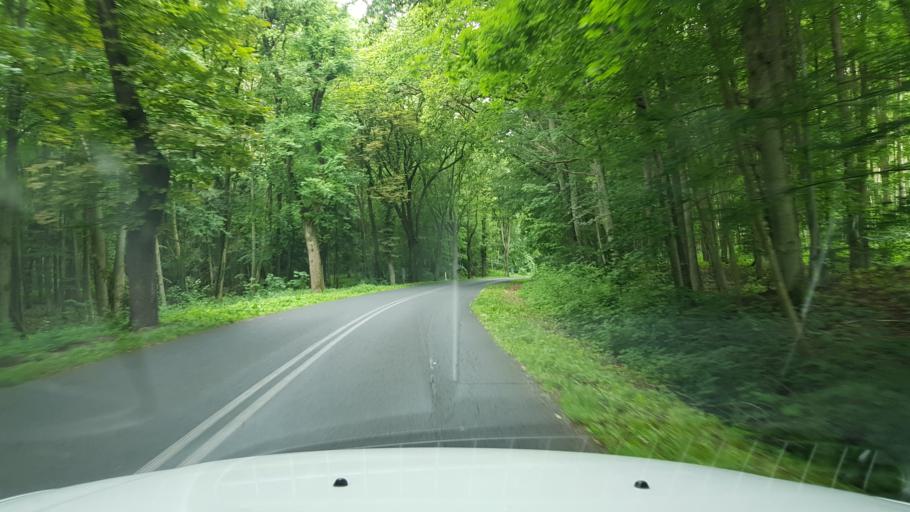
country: PL
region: West Pomeranian Voivodeship
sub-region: Powiat gryficki
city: Cerkwica
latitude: 53.9283
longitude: 15.0754
